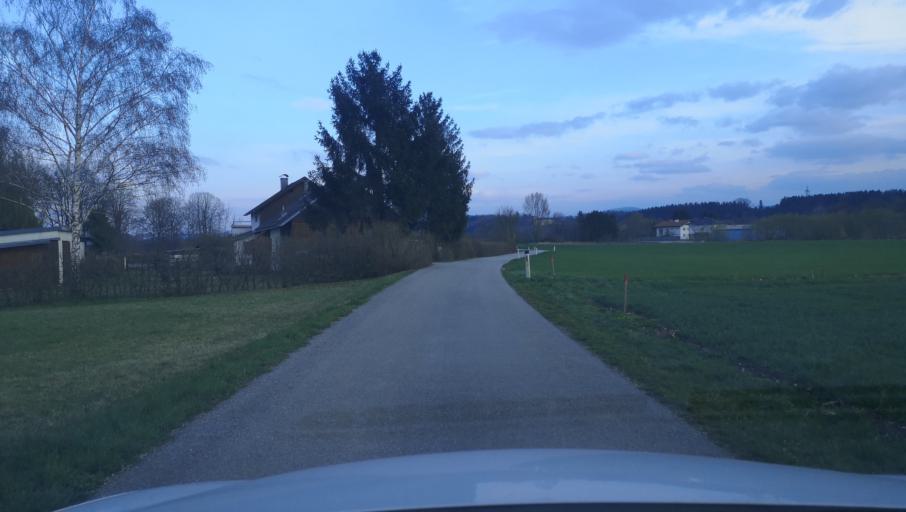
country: AT
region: Lower Austria
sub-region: Politischer Bezirk Amstetten
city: Amstetten
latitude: 48.1097
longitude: 14.8894
